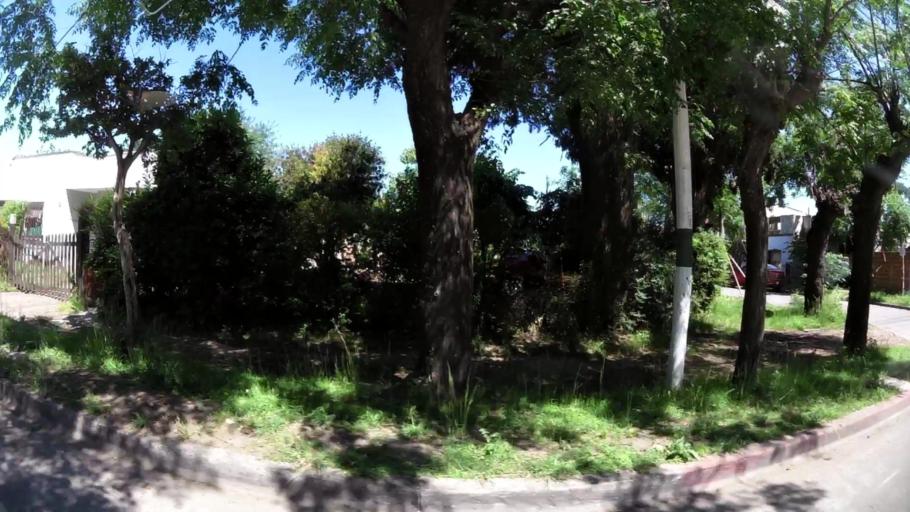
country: AR
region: Buenos Aires
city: Ituzaingo
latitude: -34.6692
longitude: -58.6607
